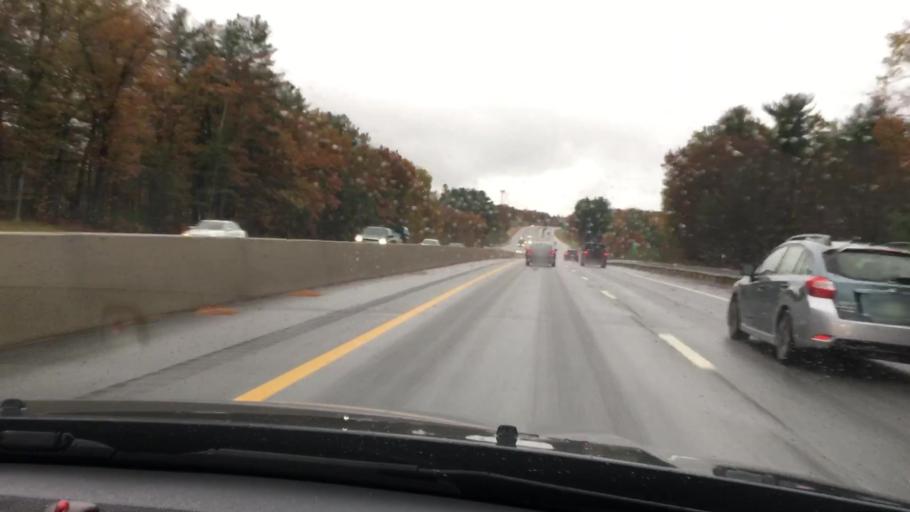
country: US
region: New Hampshire
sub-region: Hillsborough County
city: Merrimack
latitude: 42.8604
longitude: -71.5001
